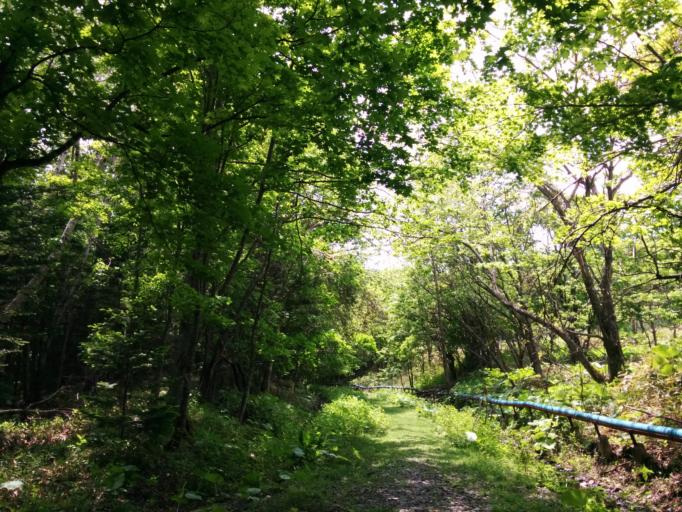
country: JP
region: Hokkaido
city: Otofuke
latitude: 43.3674
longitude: 143.1936
